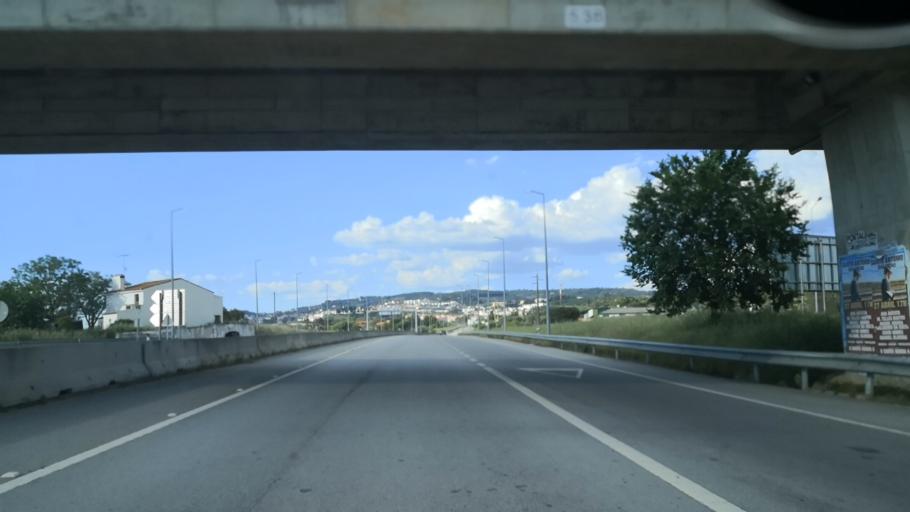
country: PT
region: Portalegre
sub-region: Portalegre
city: Portalegre
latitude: 39.2688
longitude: -7.4404
